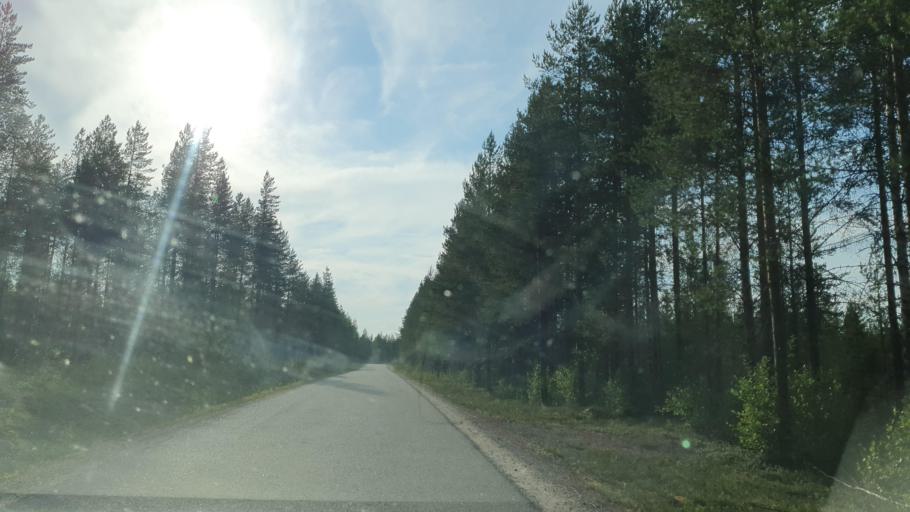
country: FI
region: Kainuu
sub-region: Kehys-Kainuu
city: Kuhmo
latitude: 64.2763
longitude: 29.4374
